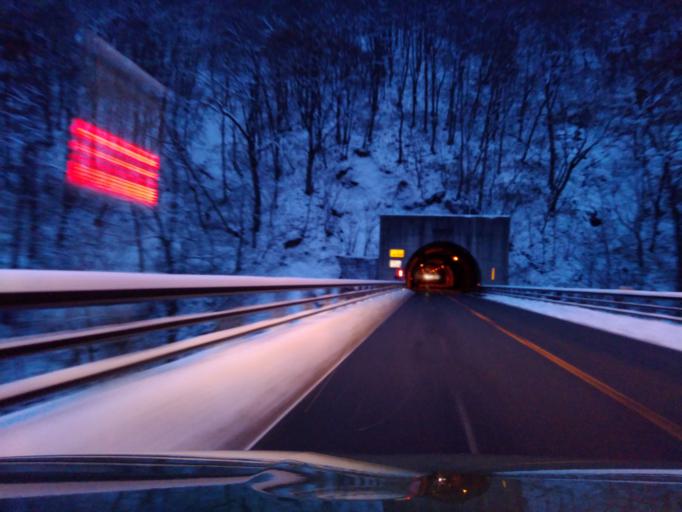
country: JP
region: Iwate
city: Shizukuishi
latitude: 39.6889
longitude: 140.7914
